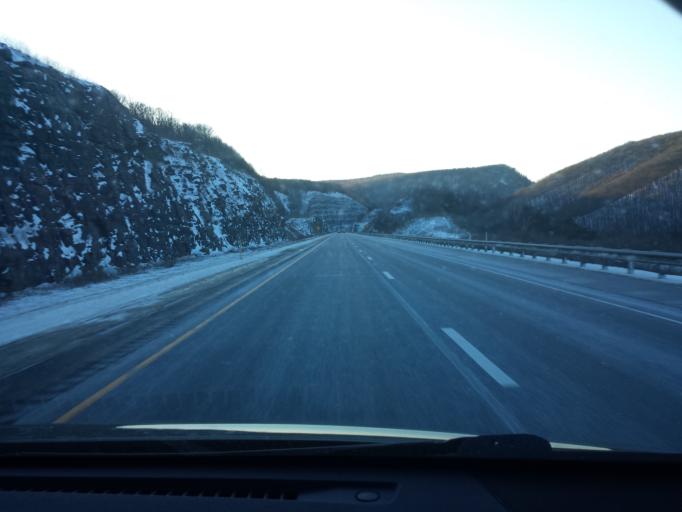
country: US
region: Pennsylvania
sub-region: Clinton County
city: Castanea
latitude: 41.0619
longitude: -77.3754
